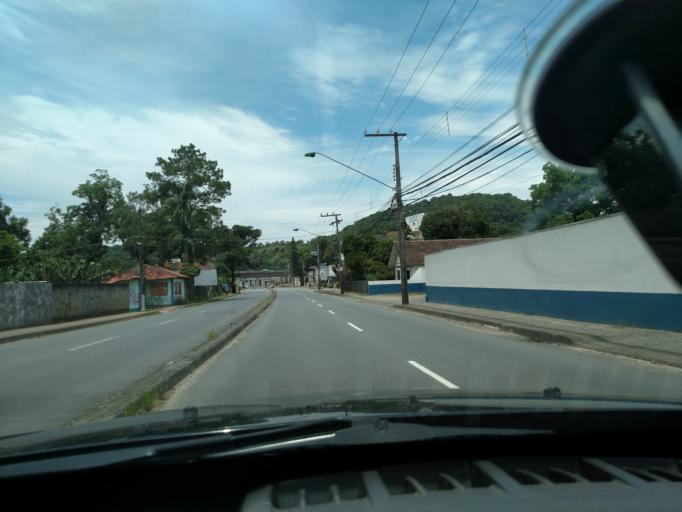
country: BR
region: Santa Catarina
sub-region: Blumenau
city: Blumenau
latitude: -26.8946
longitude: -49.0770
